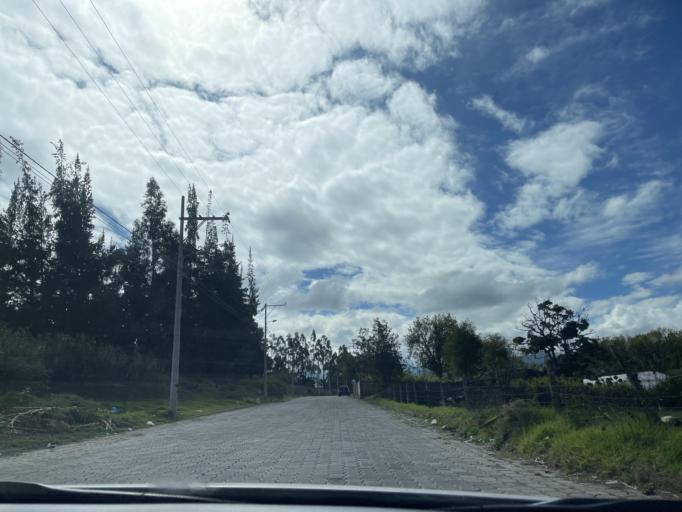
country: EC
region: Chimborazo
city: Guano
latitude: -1.6068
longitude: -78.6218
